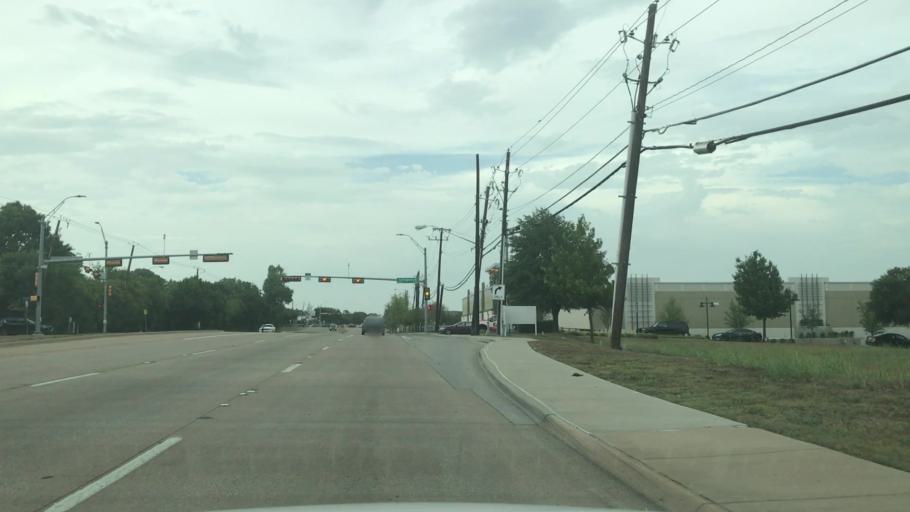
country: US
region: Texas
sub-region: Dallas County
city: University Park
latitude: 32.8751
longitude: -96.7347
